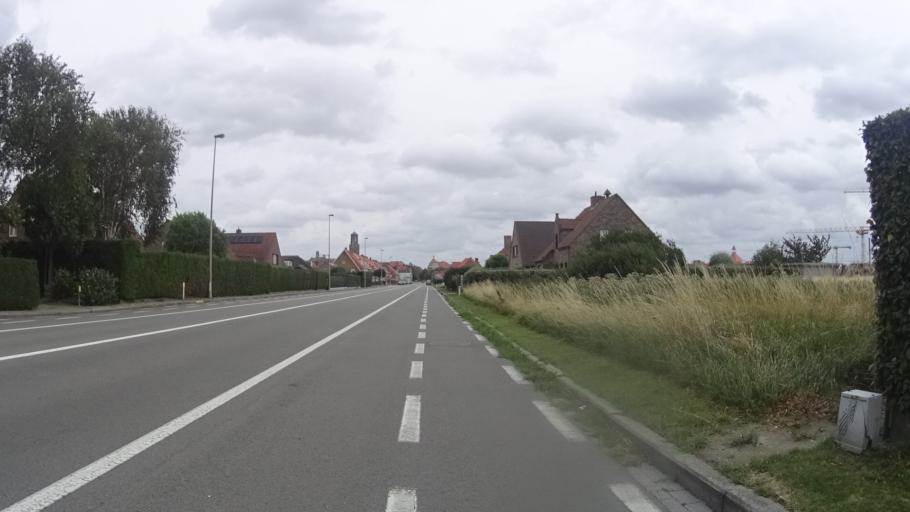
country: BE
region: Flanders
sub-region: Provincie West-Vlaanderen
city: Knokke-Heist
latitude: 51.3405
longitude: 3.2783
